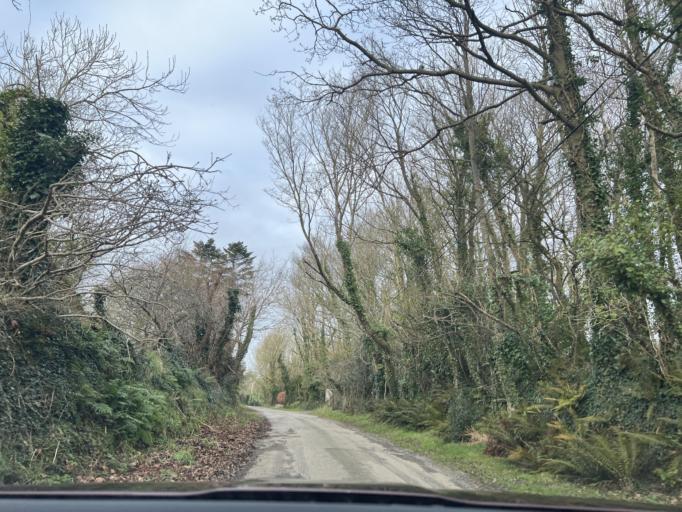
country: IE
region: Leinster
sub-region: Loch Garman
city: Loch Garman
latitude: 52.3708
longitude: -6.5354
